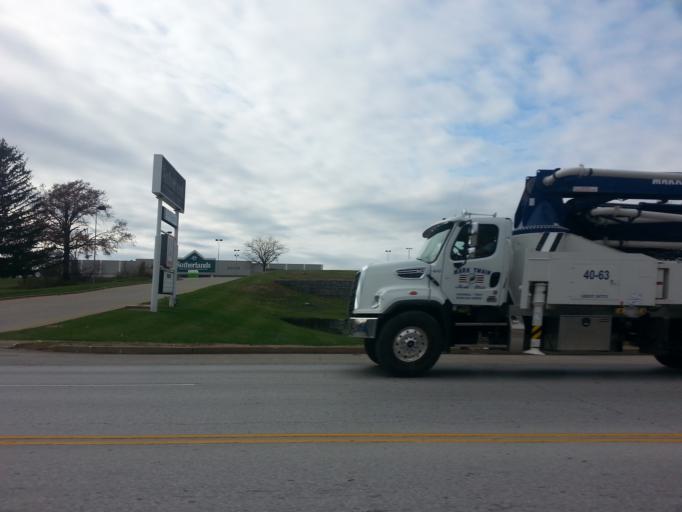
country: US
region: Missouri
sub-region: Marion County
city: Hannibal
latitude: 39.7221
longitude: -91.3919
